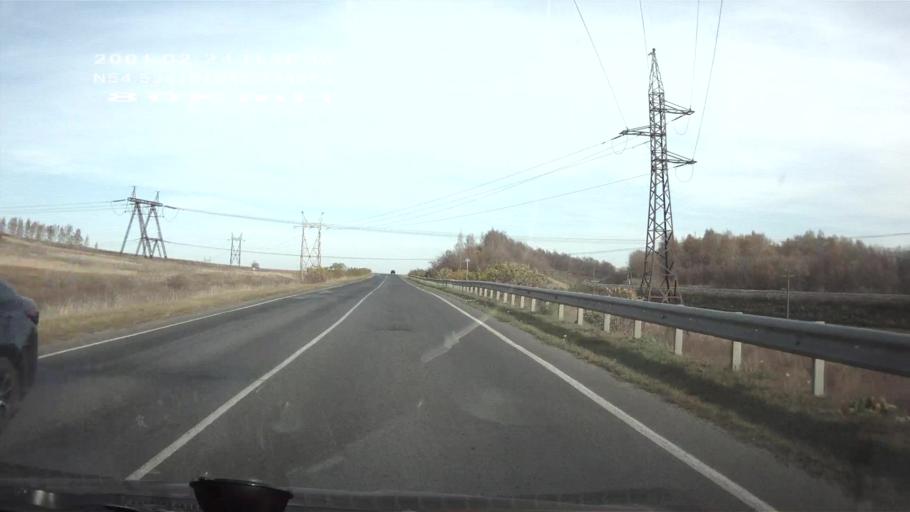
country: RU
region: Mordoviya
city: Atyashevo
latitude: 54.5343
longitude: 45.9216
